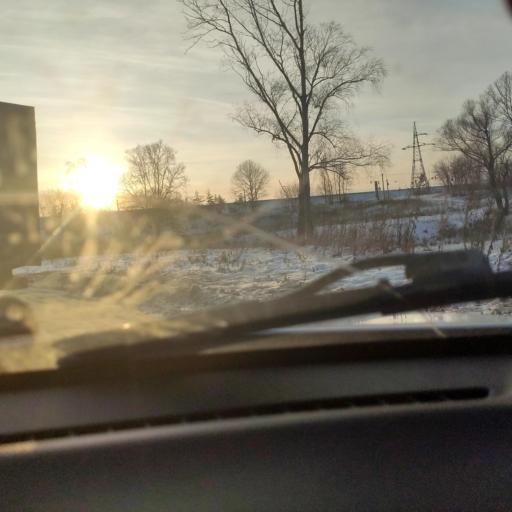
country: RU
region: Tatarstan
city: Verkhniy Uslon
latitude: 55.7992
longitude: 49.0448
